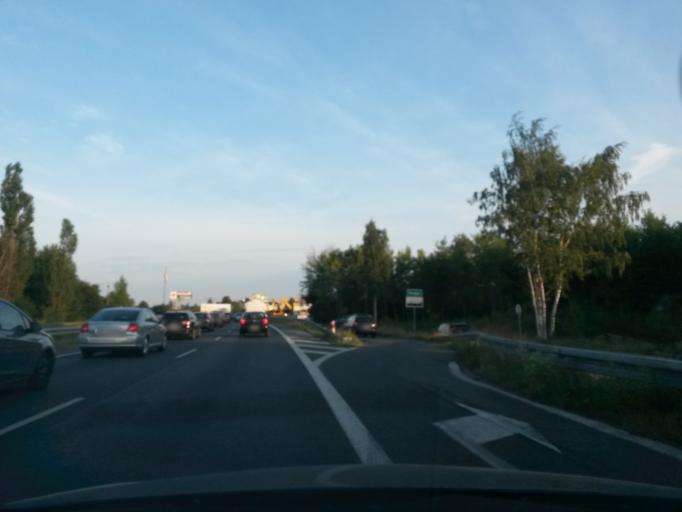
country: PL
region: Masovian Voivodeship
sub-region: Powiat warszawski zachodni
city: Kielpin
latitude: 52.3423
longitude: 20.8656
